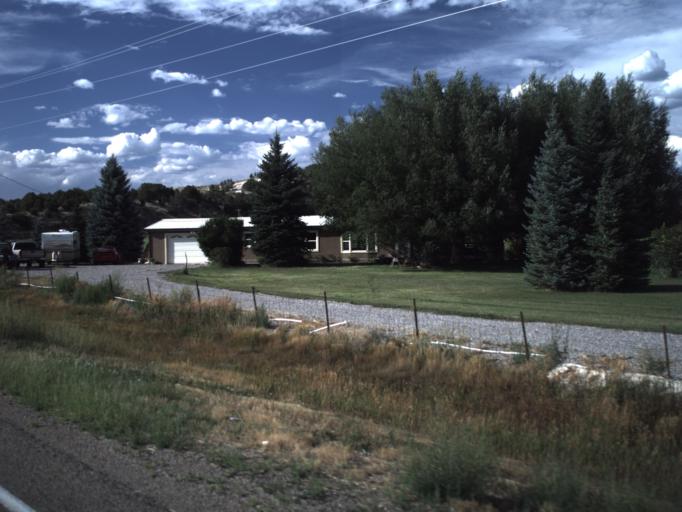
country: US
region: Utah
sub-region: Sanpete County
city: Fairview
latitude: 39.6395
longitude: -111.4472
